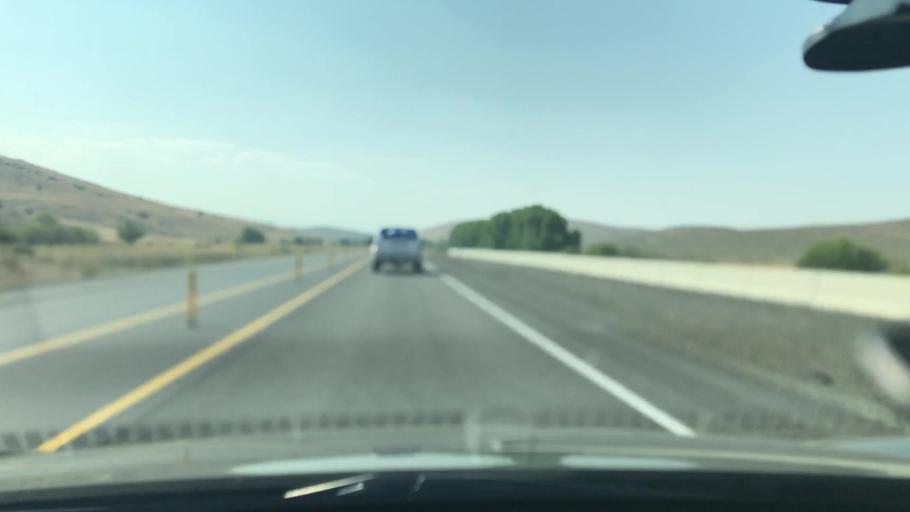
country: US
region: Oregon
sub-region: Baker County
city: Baker City
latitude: 44.6757
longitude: -117.6392
